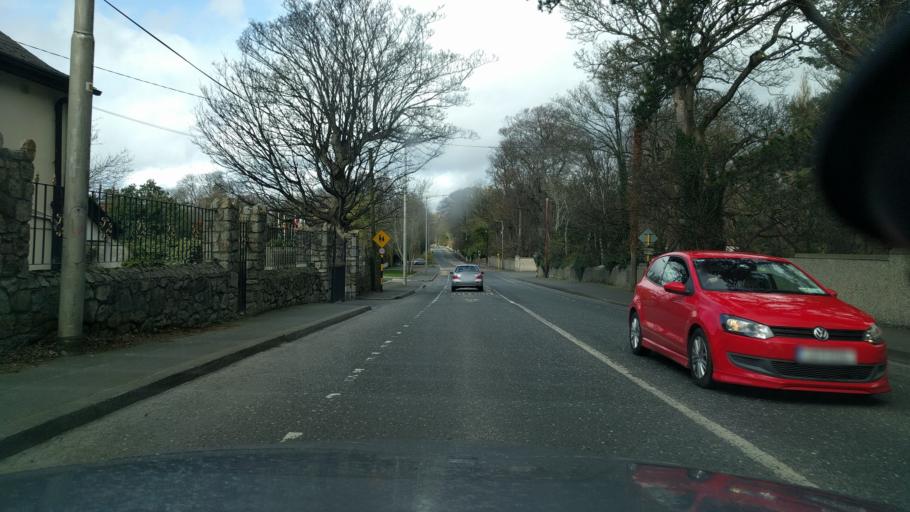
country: IE
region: Leinster
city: Little Bray
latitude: 53.2148
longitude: -6.1195
